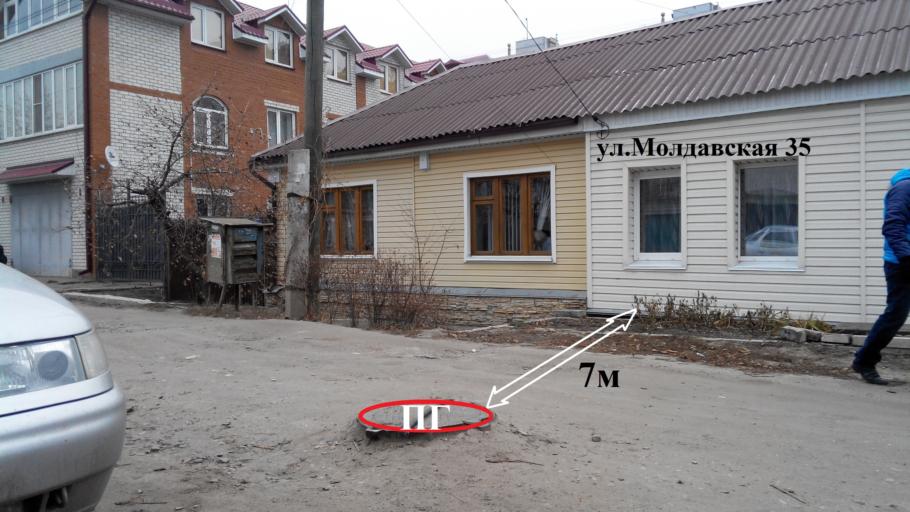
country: RU
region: Voronezj
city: Voronezh
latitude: 51.6414
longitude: 39.1654
